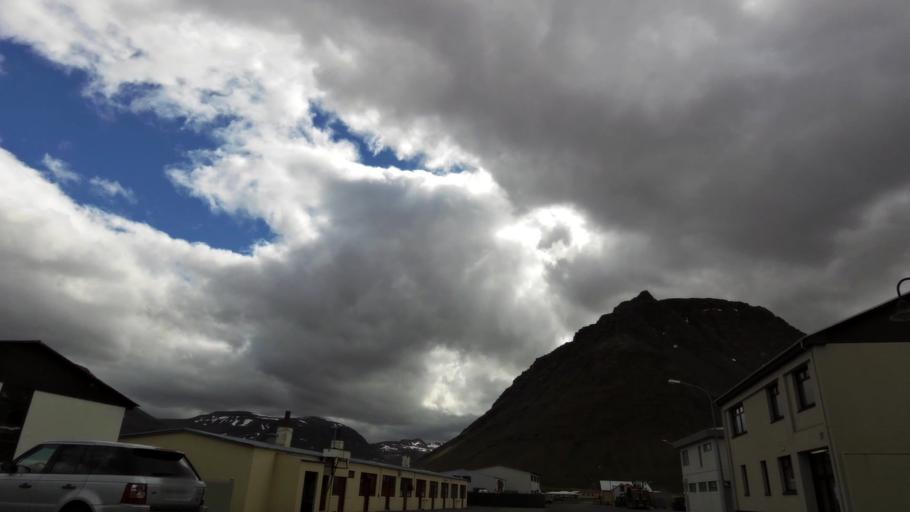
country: IS
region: Westfjords
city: Isafjoerdur
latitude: 66.1571
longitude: -23.2483
